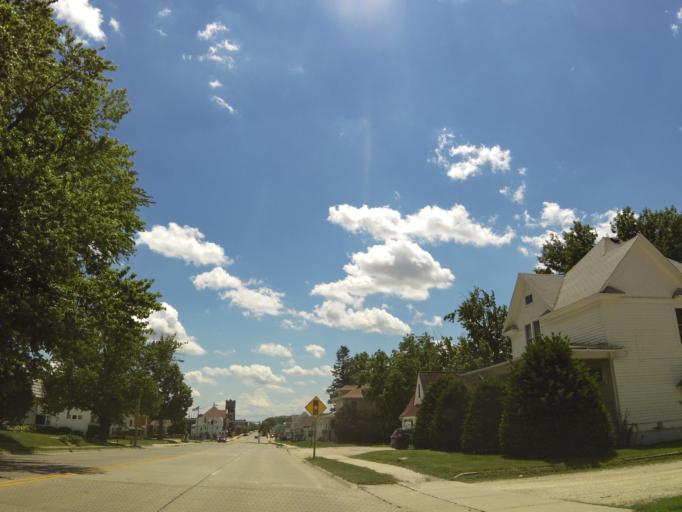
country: US
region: Iowa
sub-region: Fayette County
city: Oelwein
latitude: 42.6830
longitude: -91.9134
